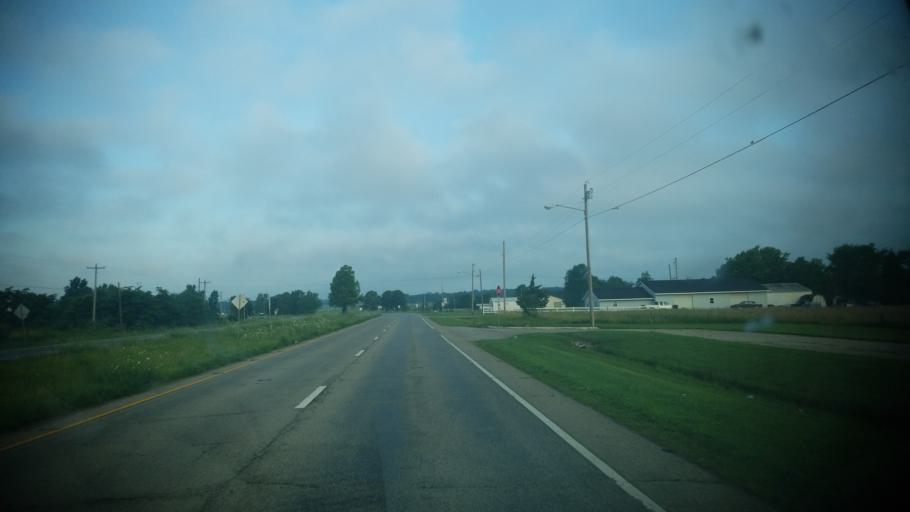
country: US
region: Illinois
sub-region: Wayne County
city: Fairfield
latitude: 38.3797
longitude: -88.3973
